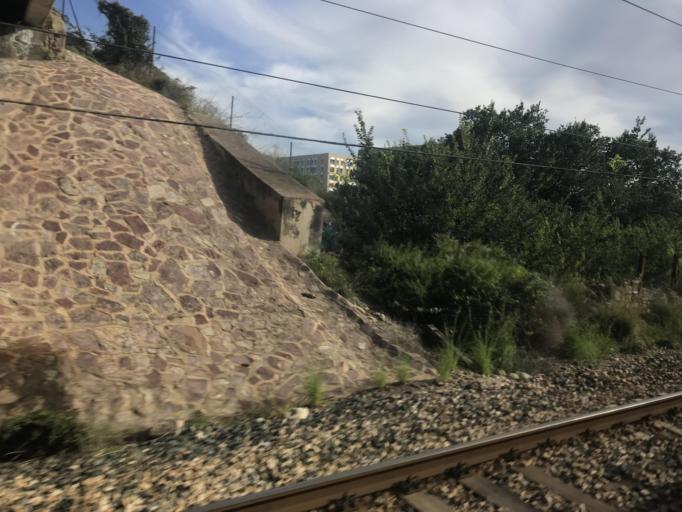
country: ES
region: Valencia
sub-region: Provincia de Castello
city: Vinaros
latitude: 40.4742
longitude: 0.4577
